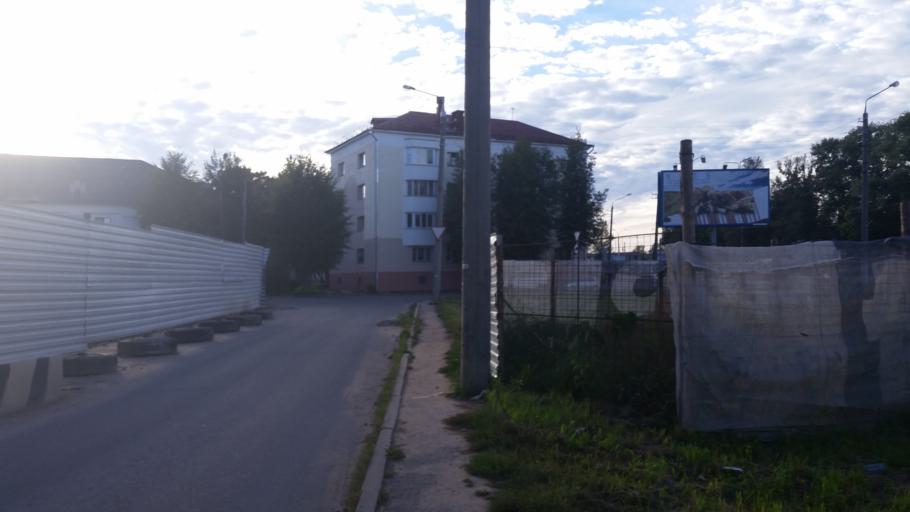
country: BY
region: Vitebsk
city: Vitebsk
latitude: 55.1845
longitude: 30.1923
